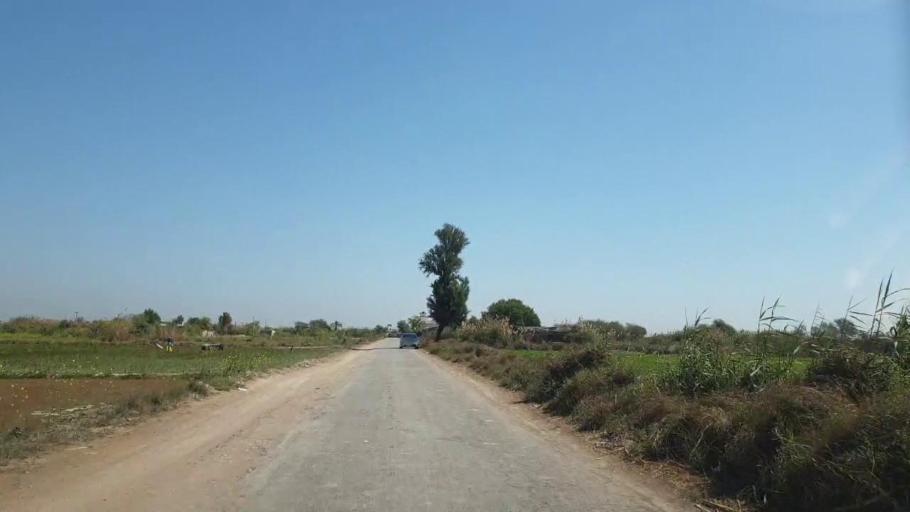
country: PK
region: Sindh
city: Mirpur Khas
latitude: 25.5964
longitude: 69.0902
